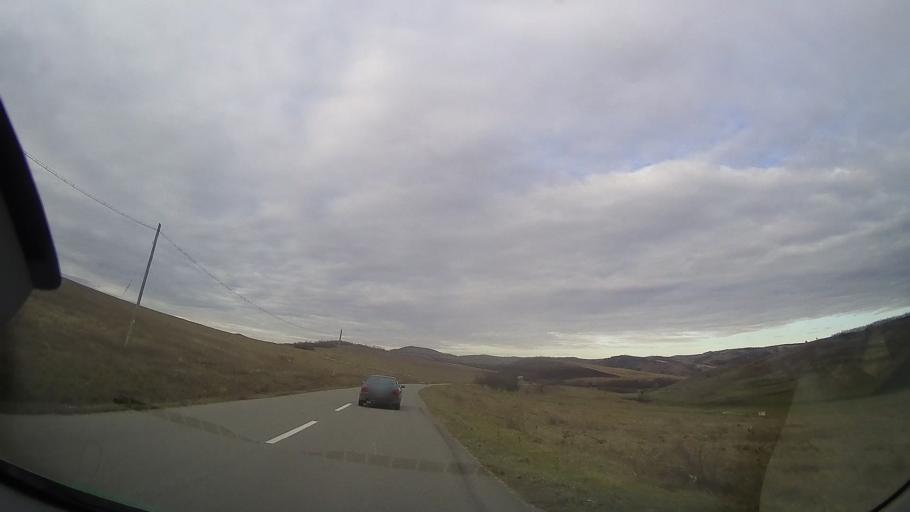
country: RO
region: Bistrita-Nasaud
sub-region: Comuna Milas
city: Milas
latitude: 46.8256
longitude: 24.4542
